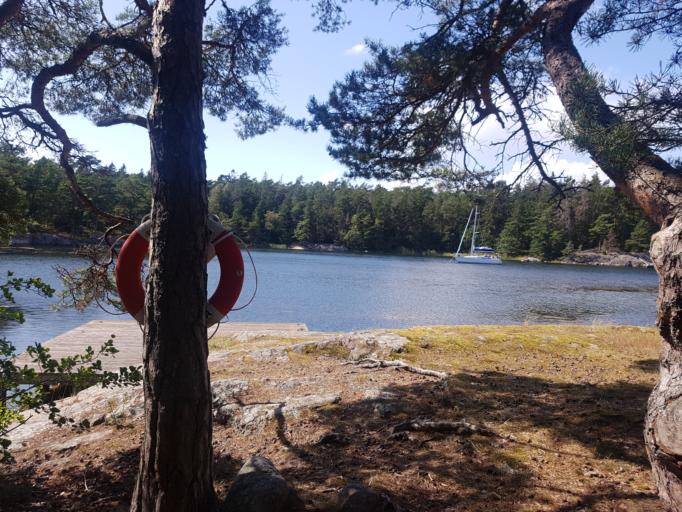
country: SE
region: Stockholm
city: Dalaro
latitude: 59.0489
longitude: 18.5226
